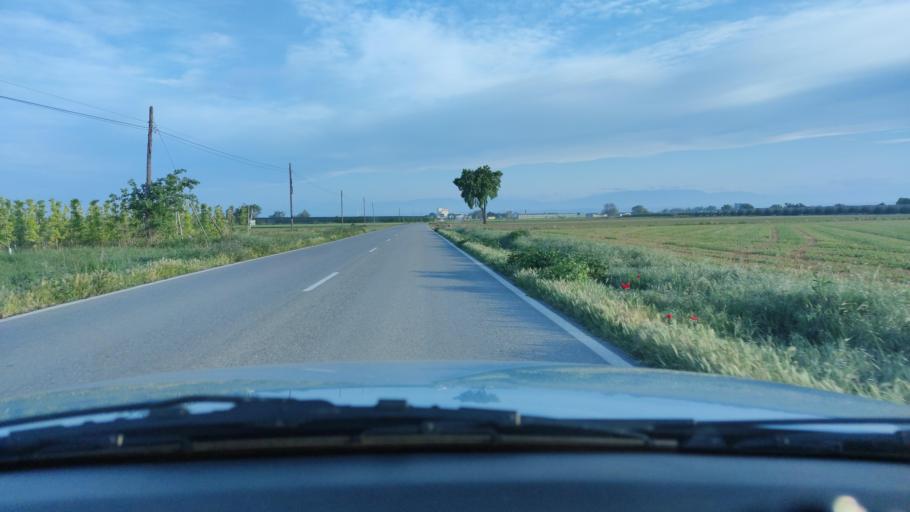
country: ES
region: Catalonia
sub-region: Provincia de Lleida
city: Ivars d'Urgell
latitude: 41.6658
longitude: 0.9924
